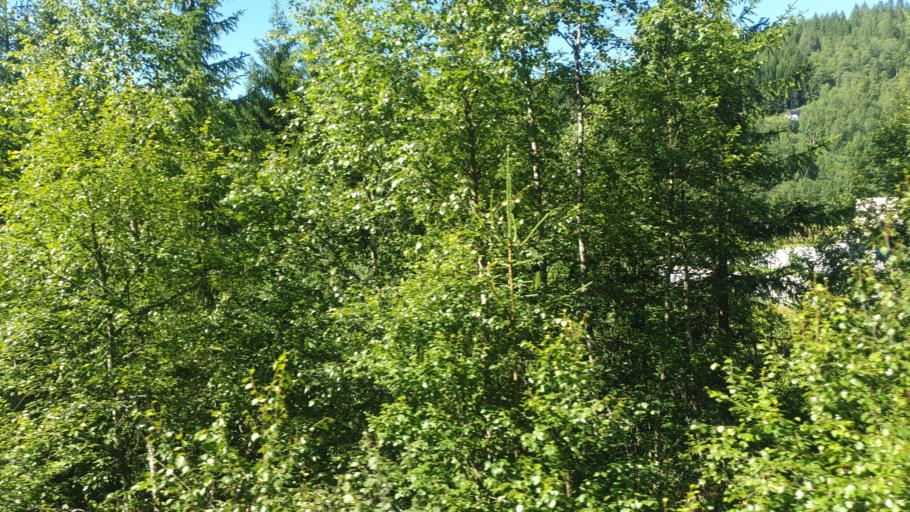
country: NO
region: Sor-Trondelag
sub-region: Meldal
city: Meldal
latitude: 63.1396
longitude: 9.7120
